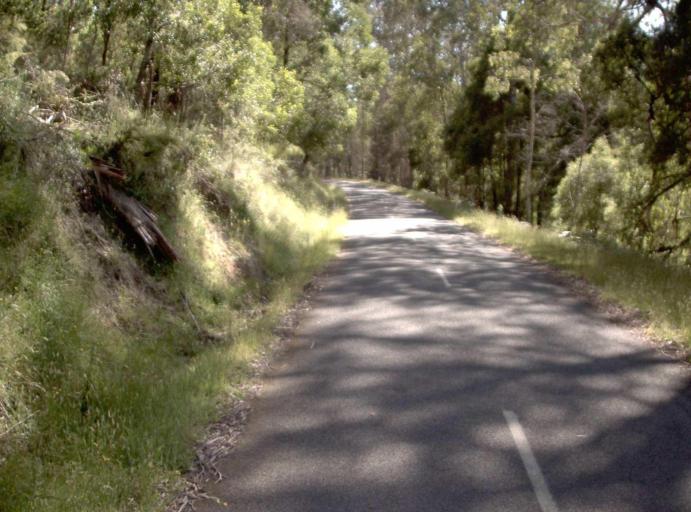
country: AU
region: New South Wales
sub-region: Bombala
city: Bombala
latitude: -37.3656
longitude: 148.6830
